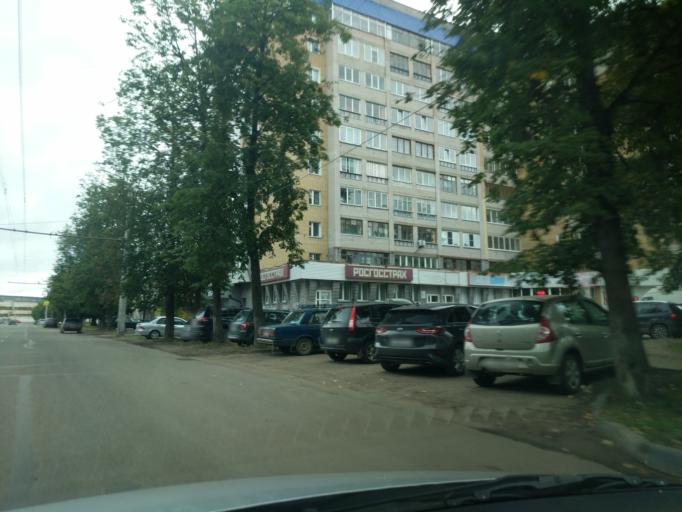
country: RU
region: Kirov
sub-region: Kirovo-Chepetskiy Rayon
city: Kirov
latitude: 58.6377
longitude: 49.6198
